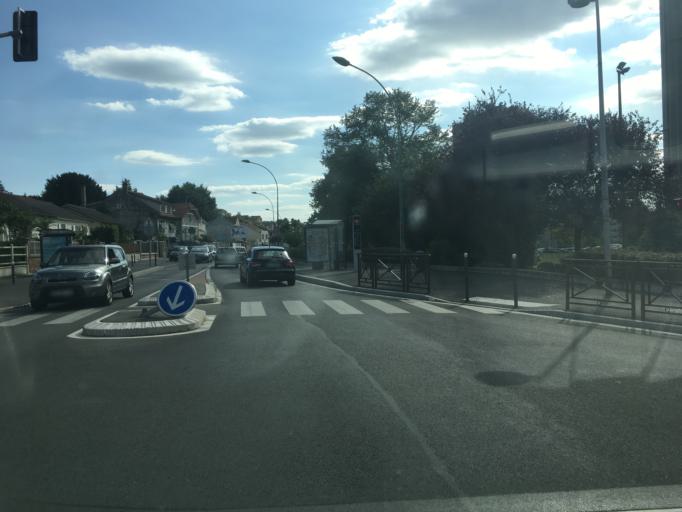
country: FR
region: Ile-de-France
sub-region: Departement du Val-de-Marne
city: Valenton
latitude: 48.7445
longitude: 2.4594
